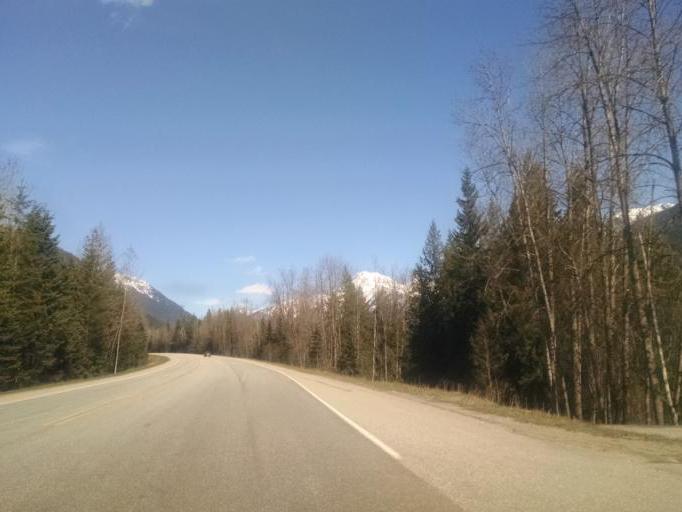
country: CA
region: British Columbia
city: Revelstoke
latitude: 51.0121
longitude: -118.0931
